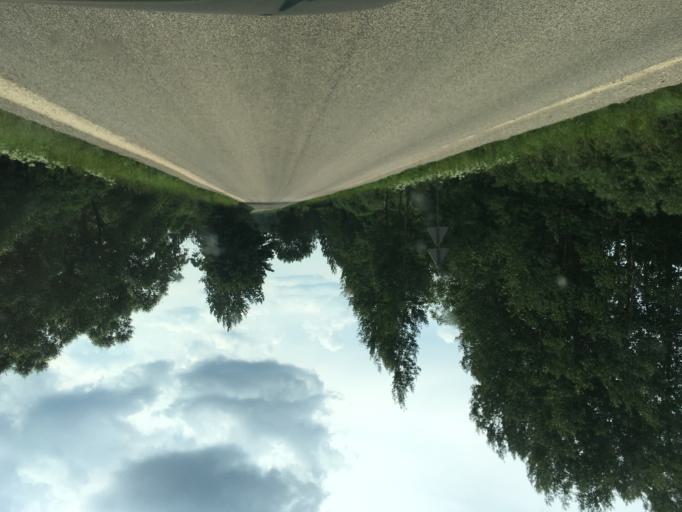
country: LV
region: Rugaju
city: Rugaji
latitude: 56.8452
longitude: 27.0919
